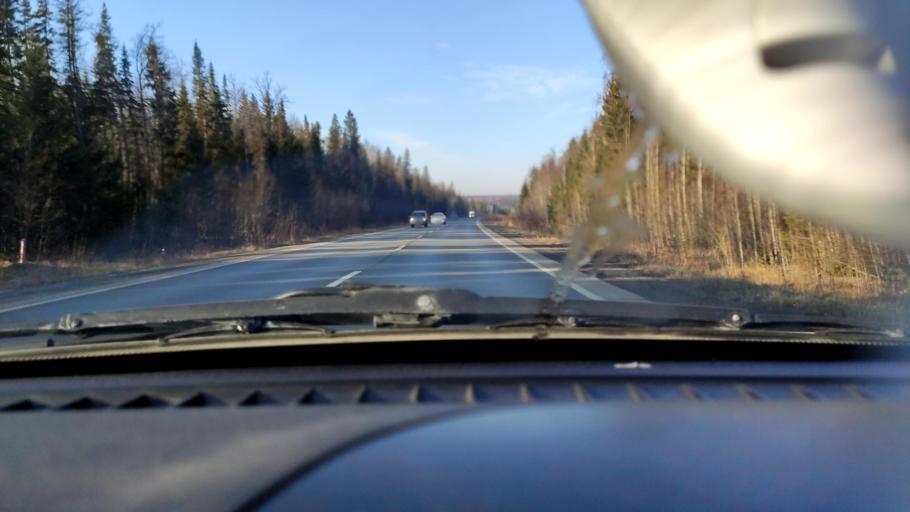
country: RU
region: Perm
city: Novyye Lyady
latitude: 58.0308
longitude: 56.4867
